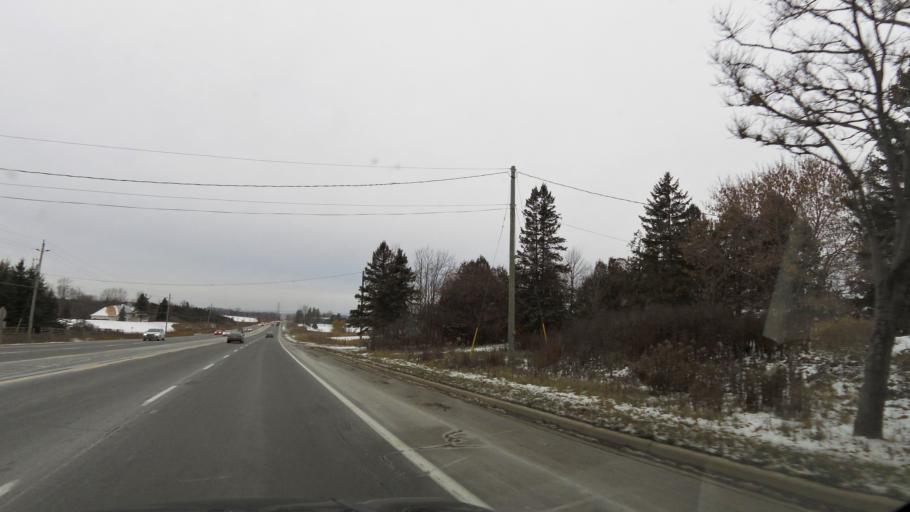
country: CA
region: Ontario
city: Newmarket
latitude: 44.0416
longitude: -79.5402
